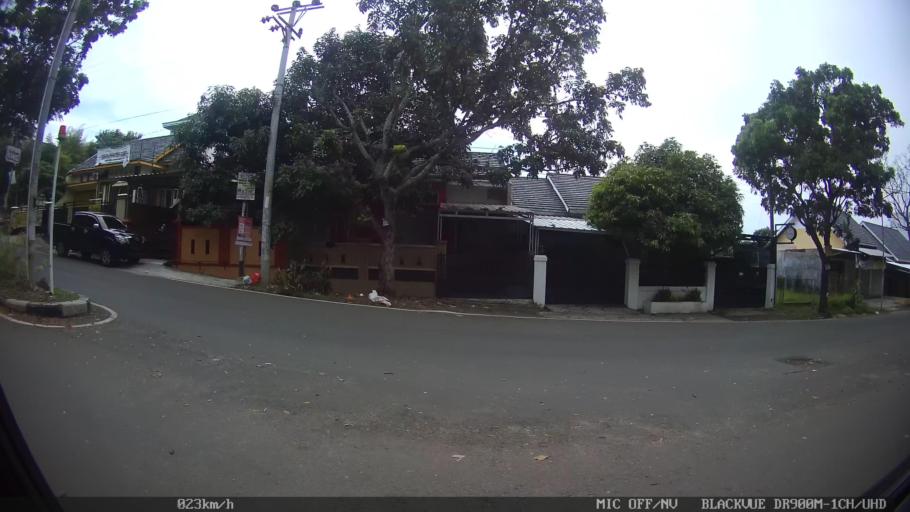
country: ID
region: Lampung
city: Kedaton
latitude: -5.3826
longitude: 105.2111
